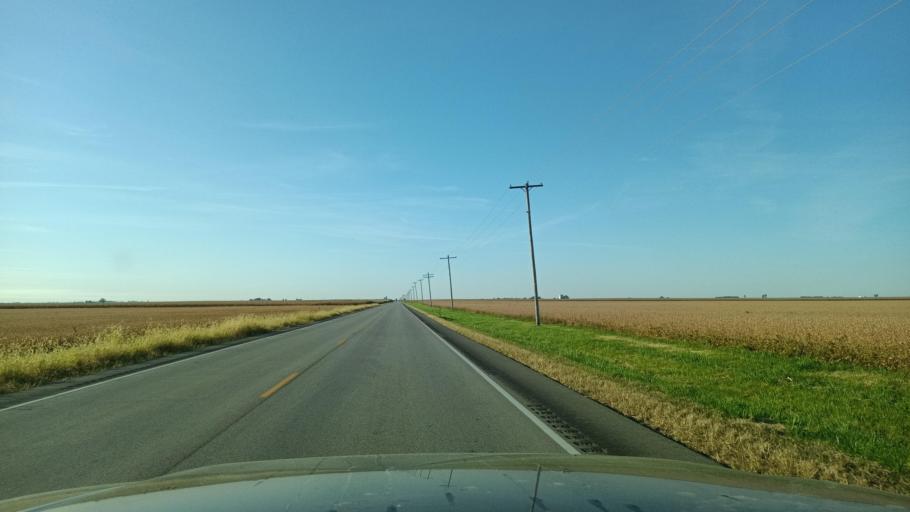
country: US
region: Illinois
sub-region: Douglas County
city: Villa Grove
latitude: 39.7877
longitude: -87.9398
